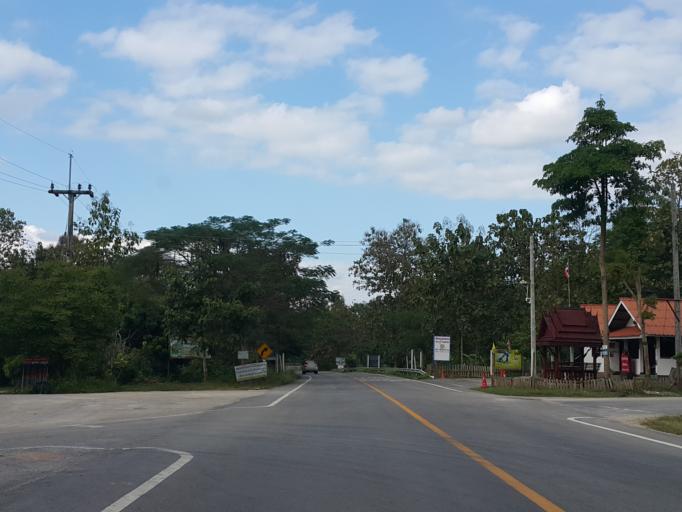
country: TH
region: Lampang
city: Chae Hom
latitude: 18.6497
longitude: 99.4939
